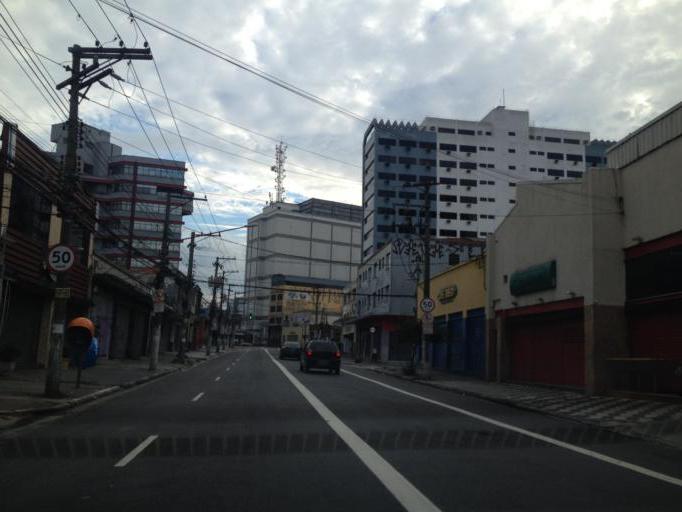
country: BR
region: Sao Paulo
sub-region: Sao Paulo
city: Sao Paulo
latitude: -23.5706
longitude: -46.6984
